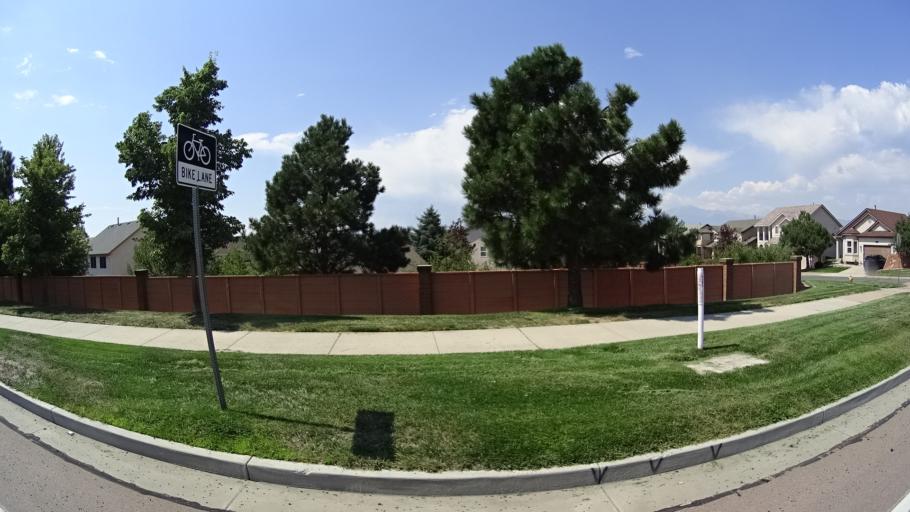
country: US
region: Colorado
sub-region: El Paso County
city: Cimarron Hills
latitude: 38.9306
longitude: -104.7382
